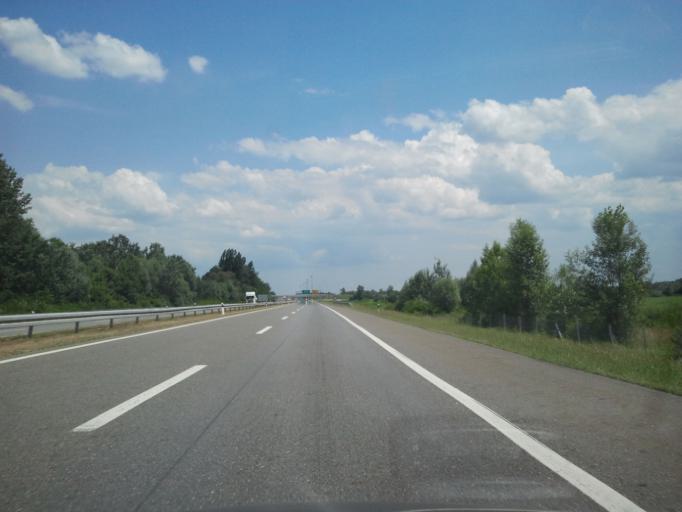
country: BA
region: Federation of Bosnia and Herzegovina
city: Donja Dubica
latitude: 45.1335
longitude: 18.3953
